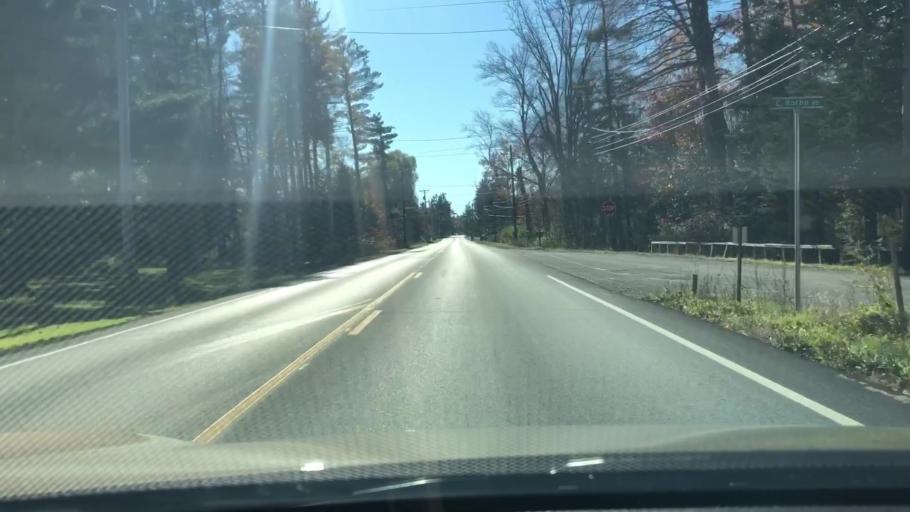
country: US
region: New York
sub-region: Ulster County
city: Zena
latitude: 42.0572
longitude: -74.0621
